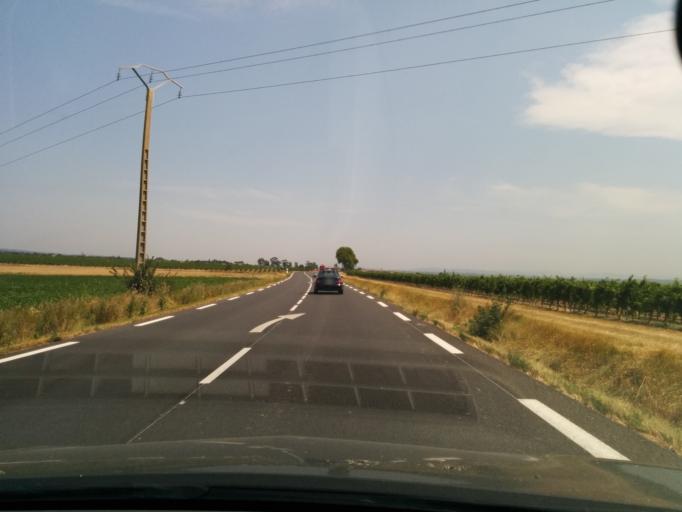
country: FR
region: Languedoc-Roussillon
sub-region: Departement de l'Aude
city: Alzonne
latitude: 43.2571
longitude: 2.1475
